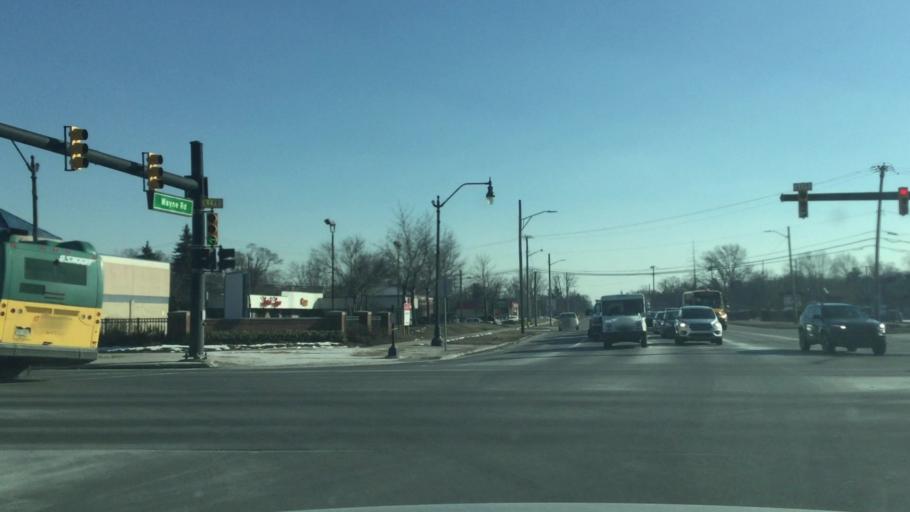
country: US
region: Michigan
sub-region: Wayne County
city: Westland
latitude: 42.3245
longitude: -83.3891
